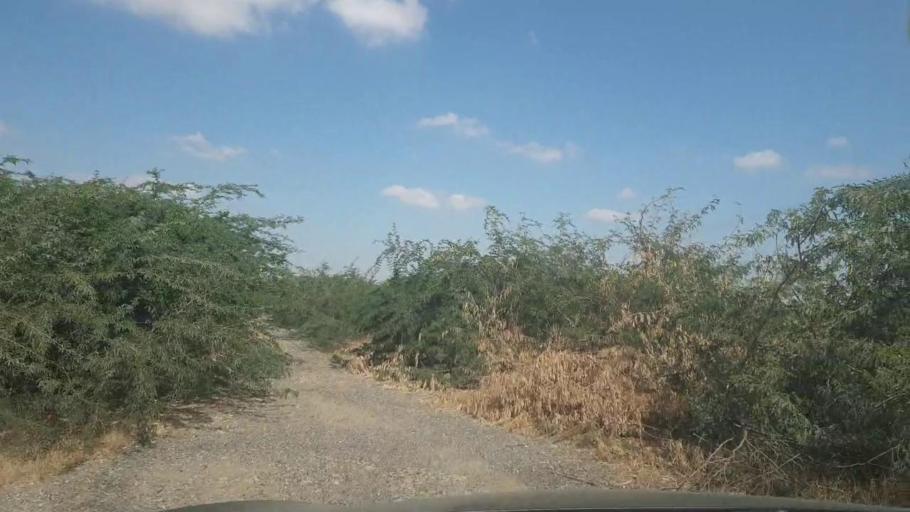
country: PK
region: Sindh
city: Malir Cantonment
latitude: 25.0646
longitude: 67.3950
